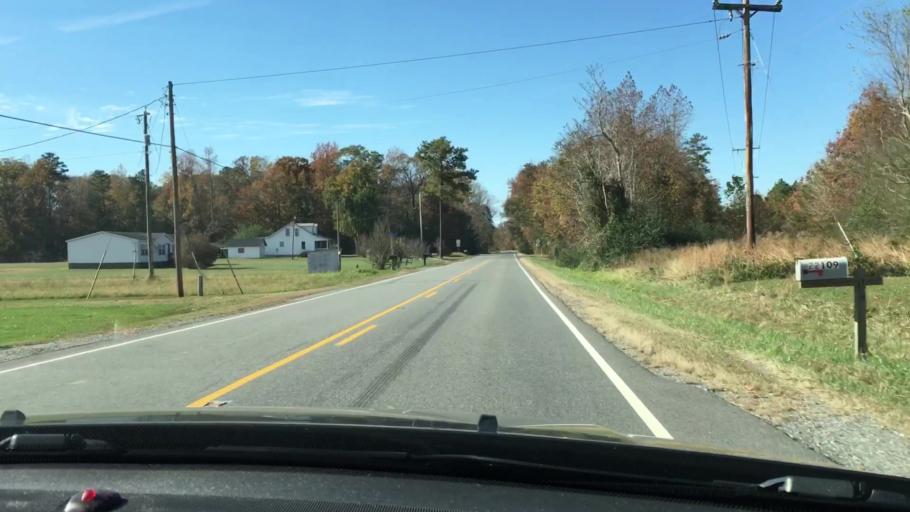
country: US
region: Virginia
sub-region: King William County
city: King William
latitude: 37.6733
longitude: -76.9773
